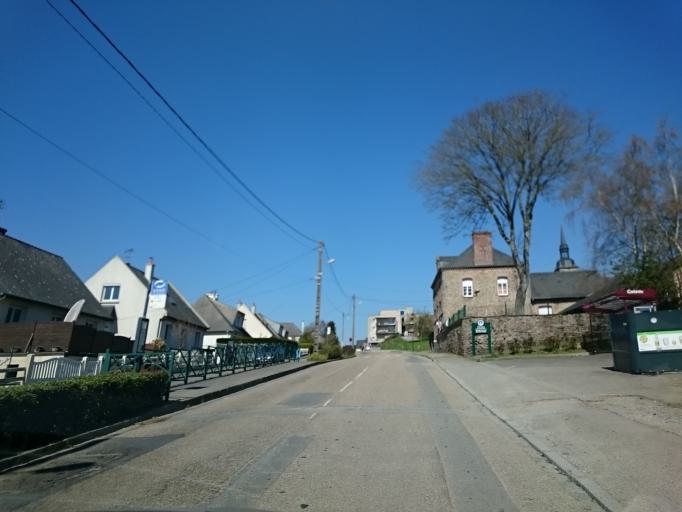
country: FR
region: Brittany
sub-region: Departement d'Ille-et-Vilaine
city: Orgeres
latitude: 47.9948
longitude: -1.6710
